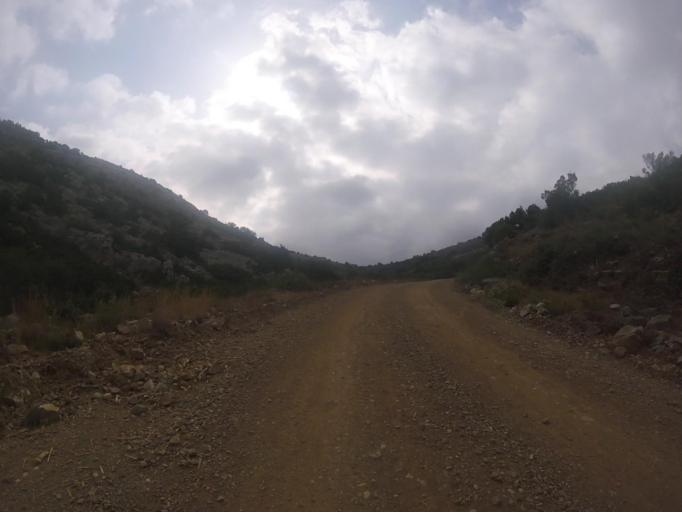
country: ES
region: Valencia
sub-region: Provincia de Castello
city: Santa Magdalena de Pulpis
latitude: 40.3465
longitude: 0.3184
